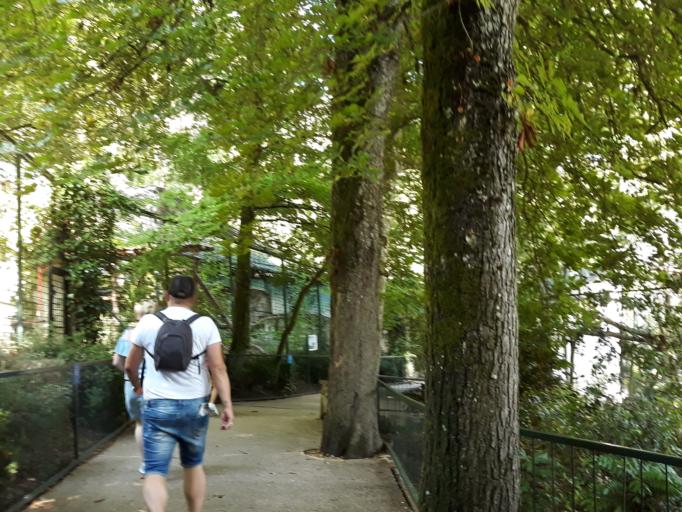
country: FR
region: Centre
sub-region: Departement du Loir-et-Cher
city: Saint-Aignan
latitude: 47.2476
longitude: 1.3497
